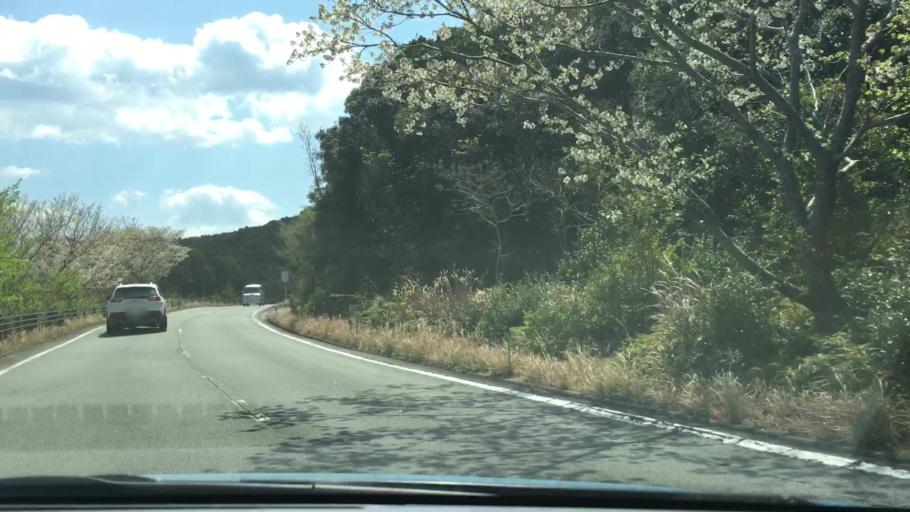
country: JP
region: Mie
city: Toba
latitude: 34.4499
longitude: 136.9059
